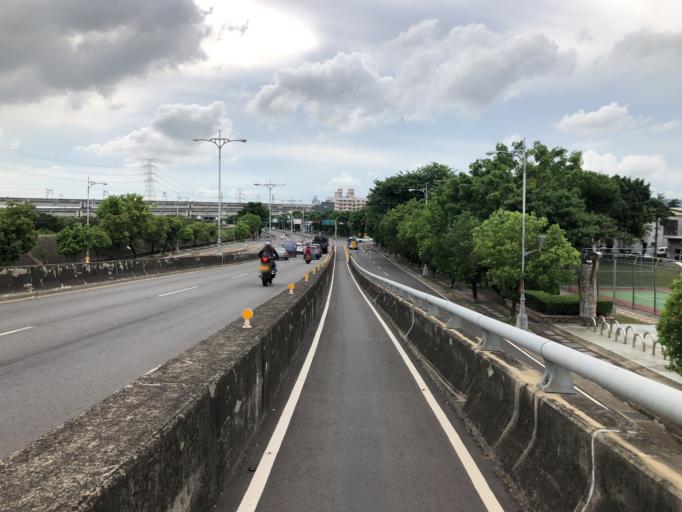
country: TW
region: Taiwan
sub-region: Changhua
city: Chang-hua
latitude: 24.1023
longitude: 120.6204
